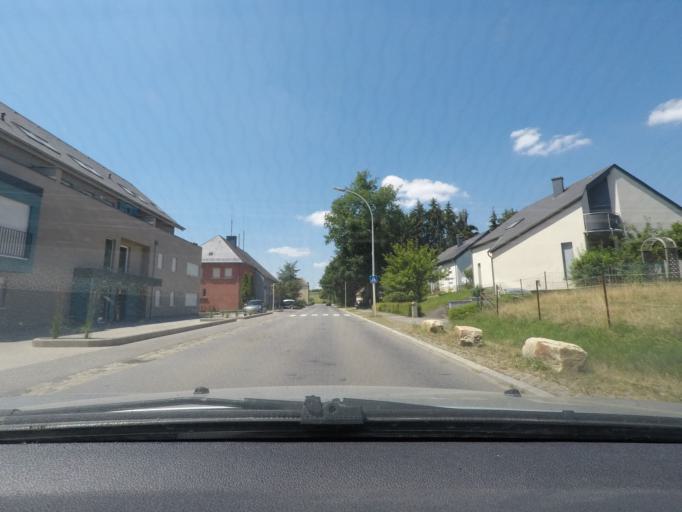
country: LU
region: Diekirch
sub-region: Canton de Redange
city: Redange-sur-Attert
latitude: 49.7661
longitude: 5.8783
